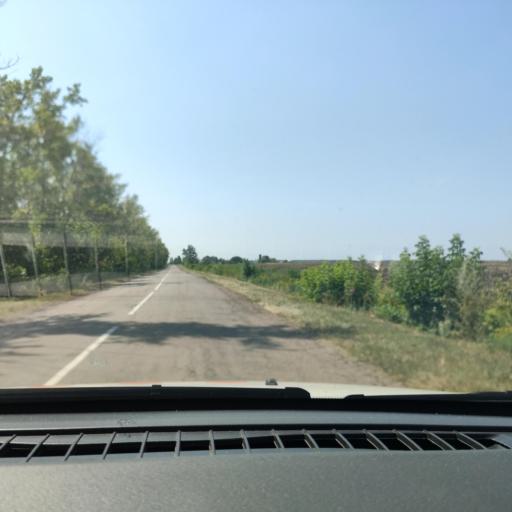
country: RU
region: Voronezj
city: Ostrogozhsk
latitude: 50.7121
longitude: 39.3390
